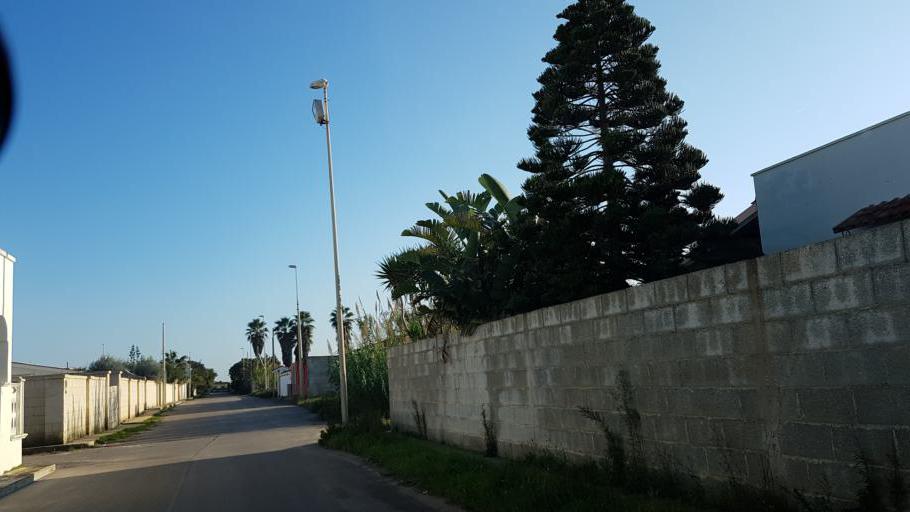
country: IT
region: Apulia
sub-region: Provincia di Brindisi
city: Torchiarolo
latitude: 40.5144
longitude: 18.0970
